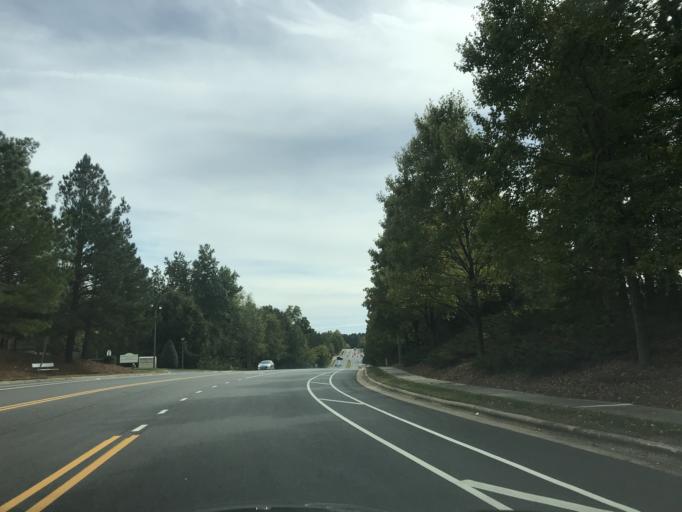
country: US
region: North Carolina
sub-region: Wake County
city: Wake Forest
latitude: 35.9481
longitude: -78.5452
